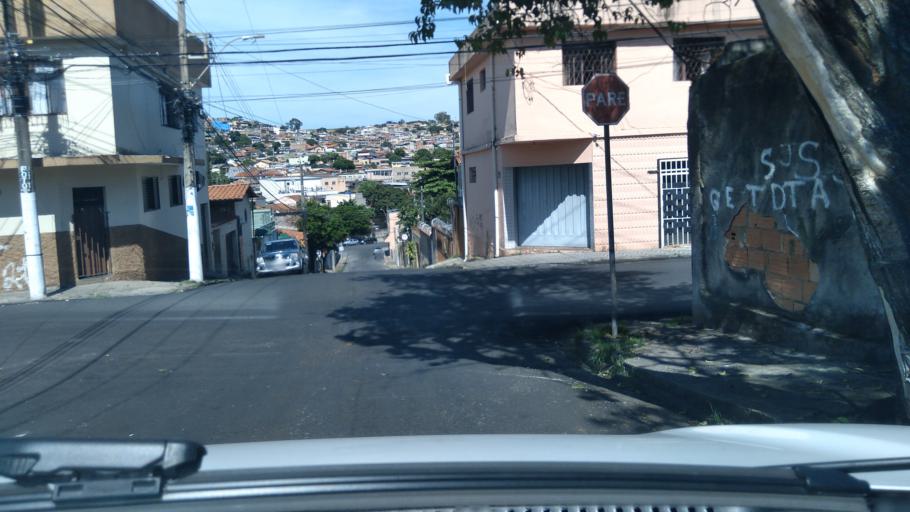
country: BR
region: Minas Gerais
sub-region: Contagem
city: Contagem
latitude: -19.9106
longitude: -44.0005
